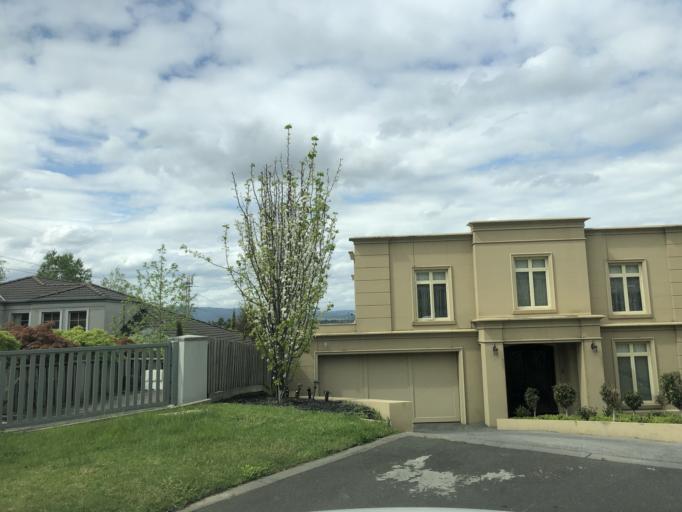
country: AU
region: Victoria
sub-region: Monash
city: Mulgrave
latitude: -37.9319
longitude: 145.2014
